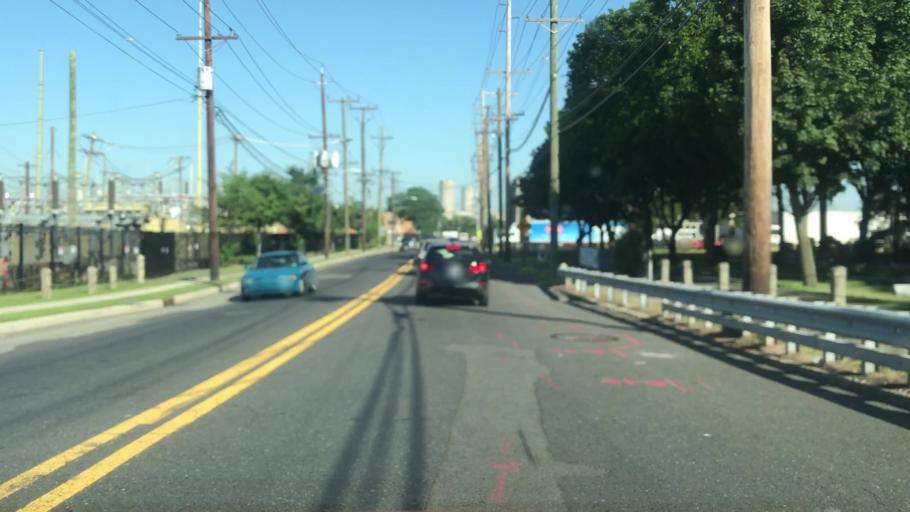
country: US
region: New Jersey
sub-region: Bergen County
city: Ridgefield
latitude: 40.8339
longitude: -74.0140
